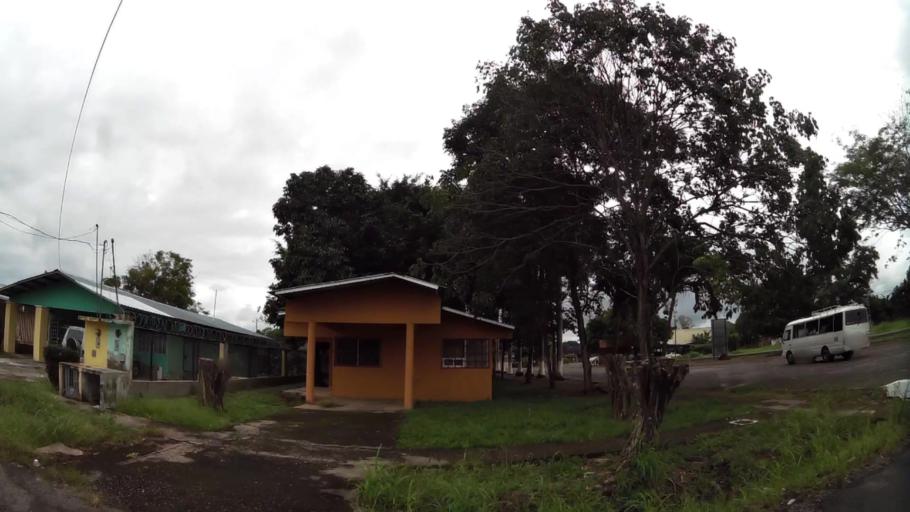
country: PA
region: Chiriqui
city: David
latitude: 8.4015
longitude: -82.4595
